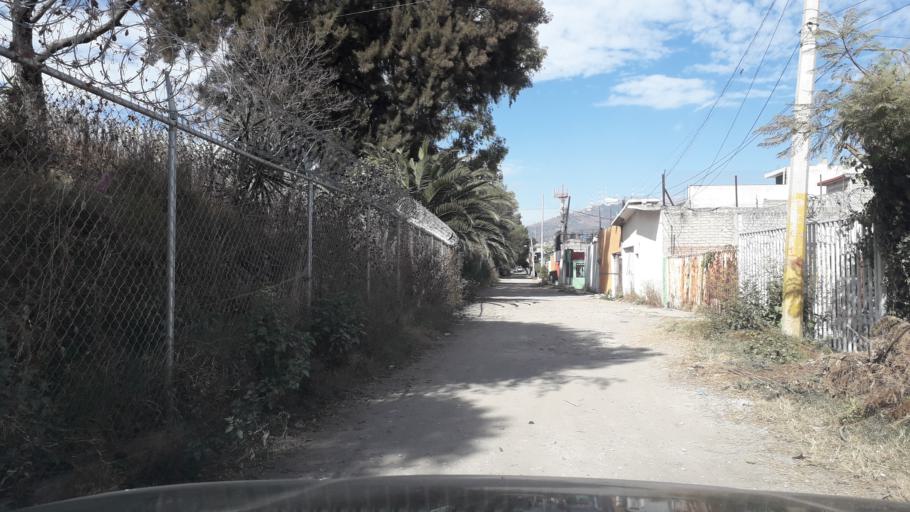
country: MX
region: Mexico City
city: Gustavo A. Madero
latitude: 19.5087
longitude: -99.0874
